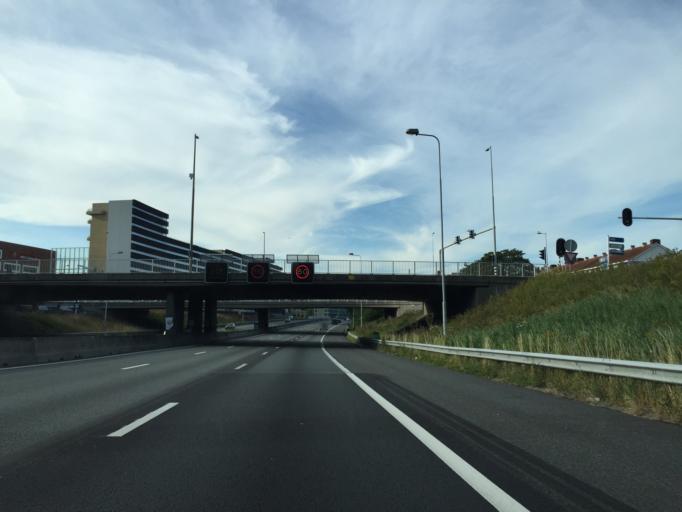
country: NL
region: North Holland
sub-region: Gemeente Amsterdam
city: Amsterdam
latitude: 52.3714
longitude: 4.8423
